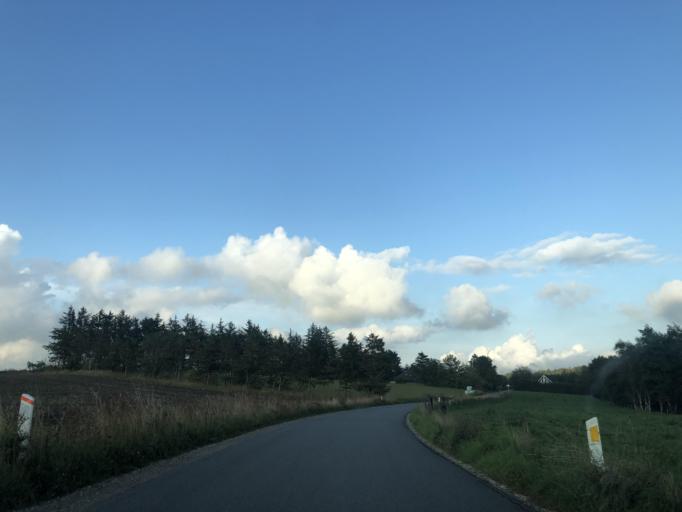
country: DK
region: North Denmark
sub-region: Alborg Kommune
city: Svenstrup
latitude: 56.9398
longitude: 9.8005
